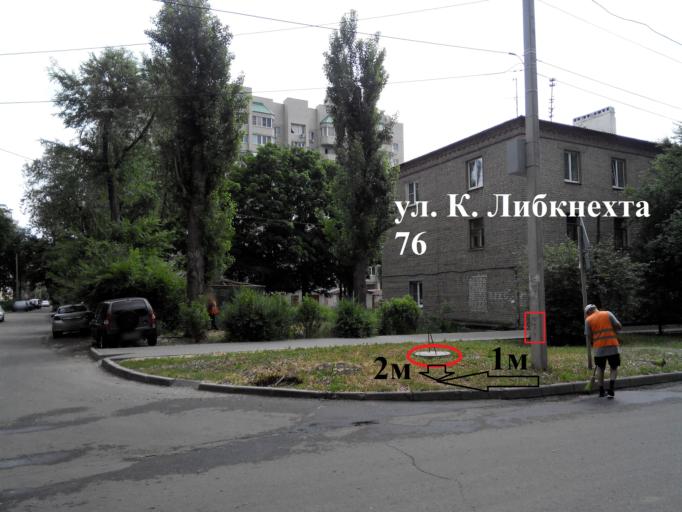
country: RU
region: Voronezj
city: Voronezh
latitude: 51.6492
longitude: 39.1710
